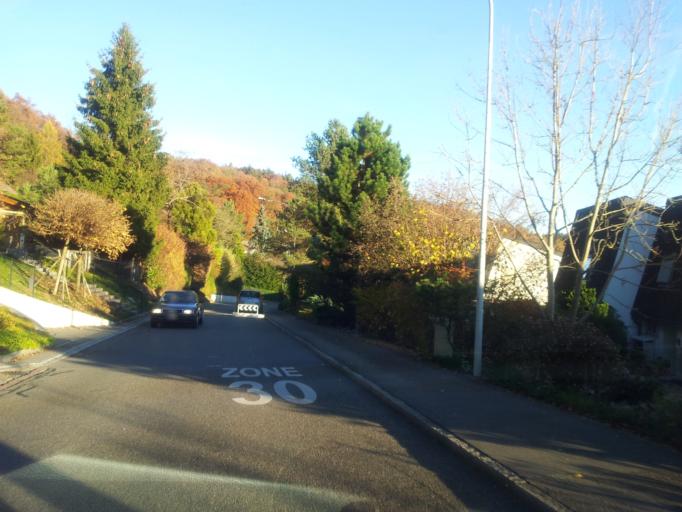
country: CH
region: Zurich
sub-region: Bezirk Dielsdorf
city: Daenikon
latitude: 47.4324
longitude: 8.3915
